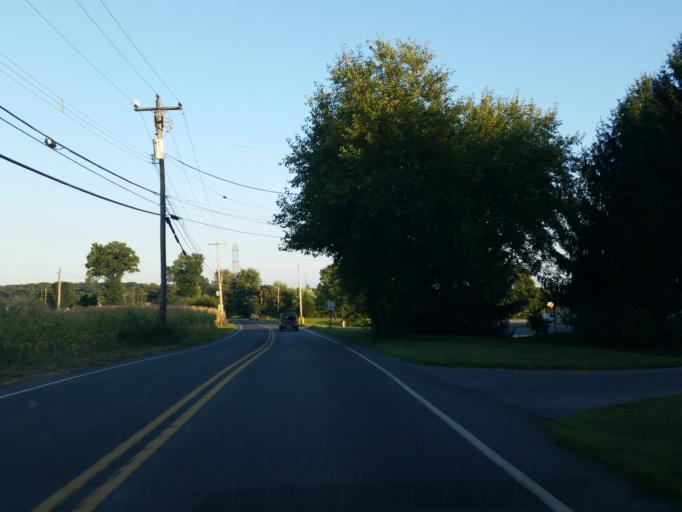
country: US
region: Pennsylvania
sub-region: Lebanon County
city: Sand Hill
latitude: 40.3772
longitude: -76.4420
